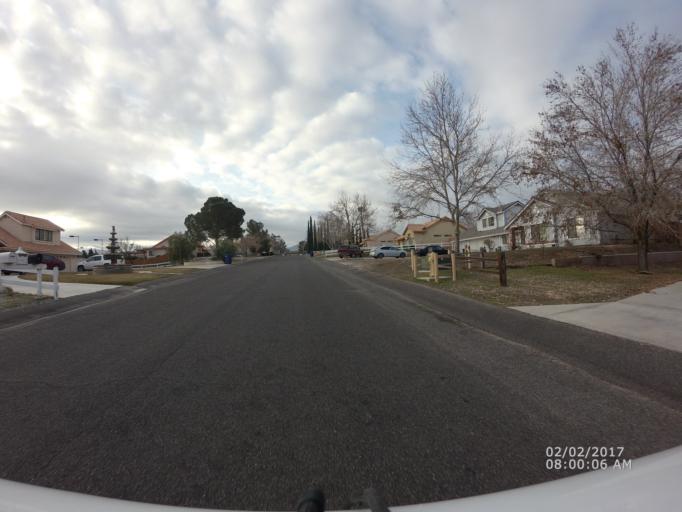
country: US
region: California
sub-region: Los Angeles County
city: Littlerock
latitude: 34.5343
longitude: -118.0437
